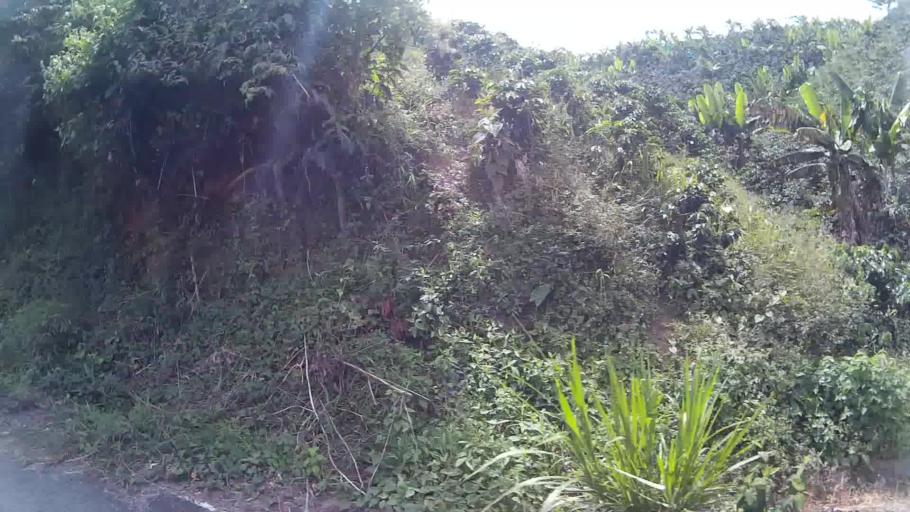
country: CO
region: Risaralda
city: Marsella
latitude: 4.8997
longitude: -75.7453
